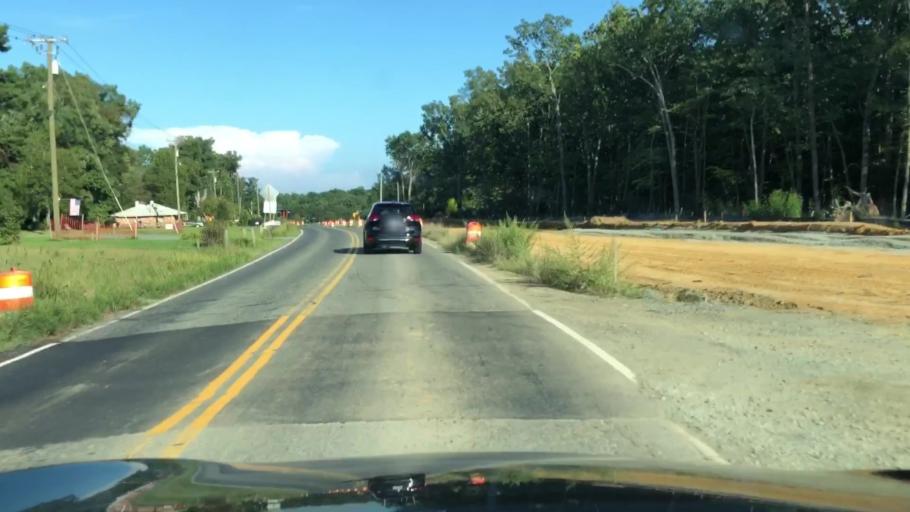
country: US
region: Virginia
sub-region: Stafford County
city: Stafford
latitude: 38.4338
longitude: -77.4466
